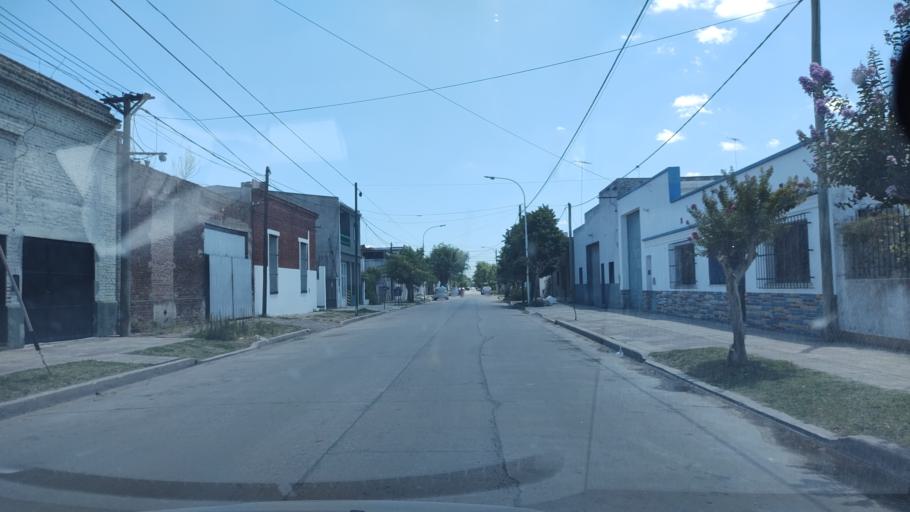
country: AR
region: Buenos Aires
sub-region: Partido de Lobos
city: Lobos
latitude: -35.1802
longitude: -59.0985
